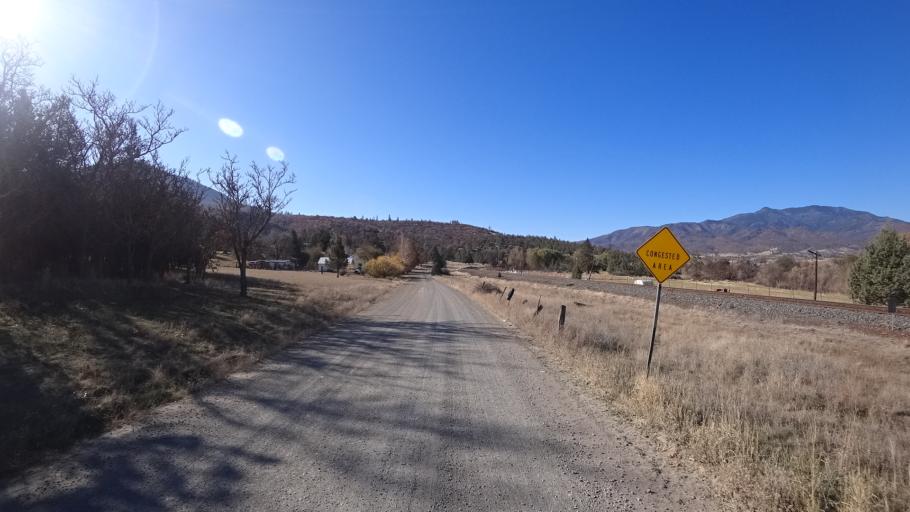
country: US
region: California
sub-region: Siskiyou County
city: Montague
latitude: 41.8965
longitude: -122.5178
